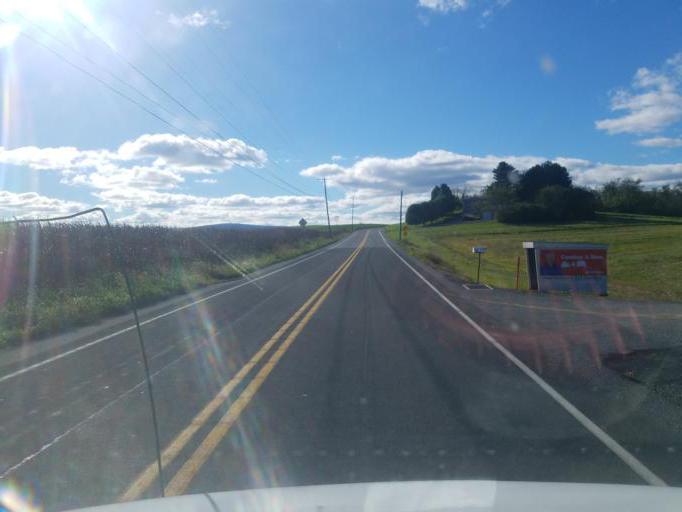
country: US
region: Pennsylvania
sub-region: Franklin County
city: Waynesboro
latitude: 39.7834
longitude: -77.5699
